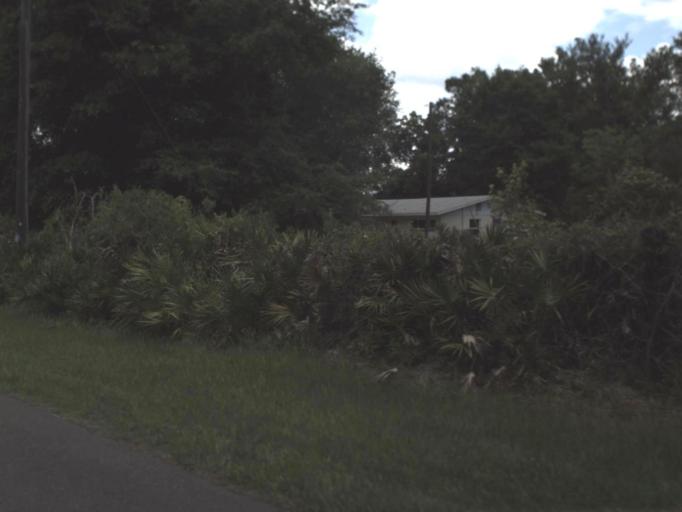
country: US
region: Florida
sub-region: Alachua County
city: Waldo
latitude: 29.7053
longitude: -82.1689
